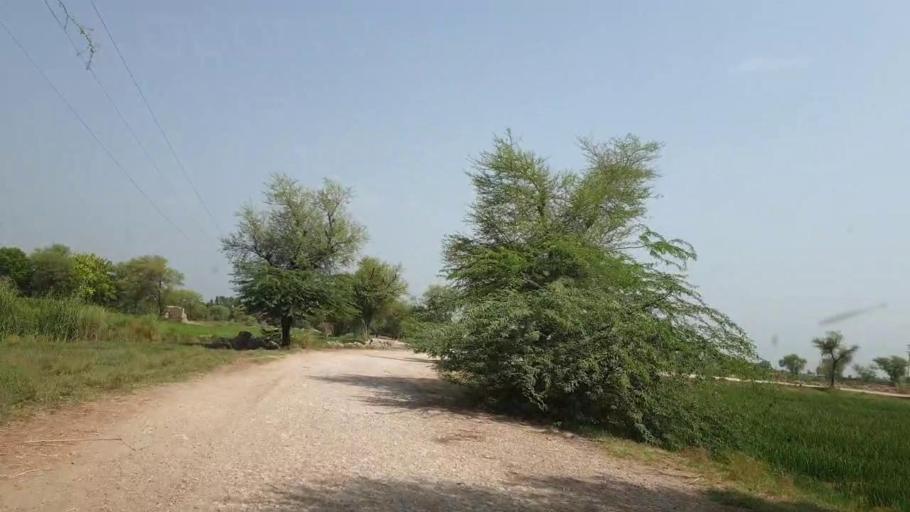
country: PK
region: Sindh
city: Lakhi
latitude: 27.8776
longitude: 68.6581
